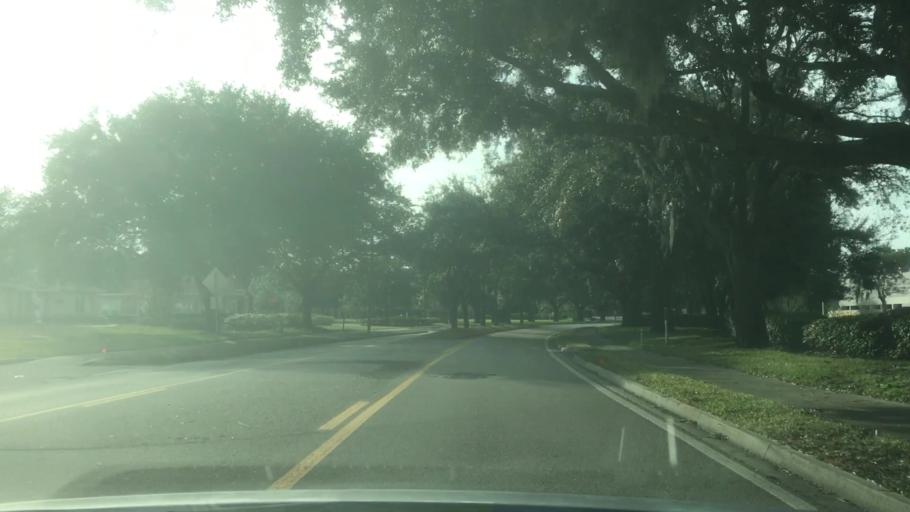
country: US
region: Florida
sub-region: Duval County
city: Jacksonville
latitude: 30.2584
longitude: -81.5891
